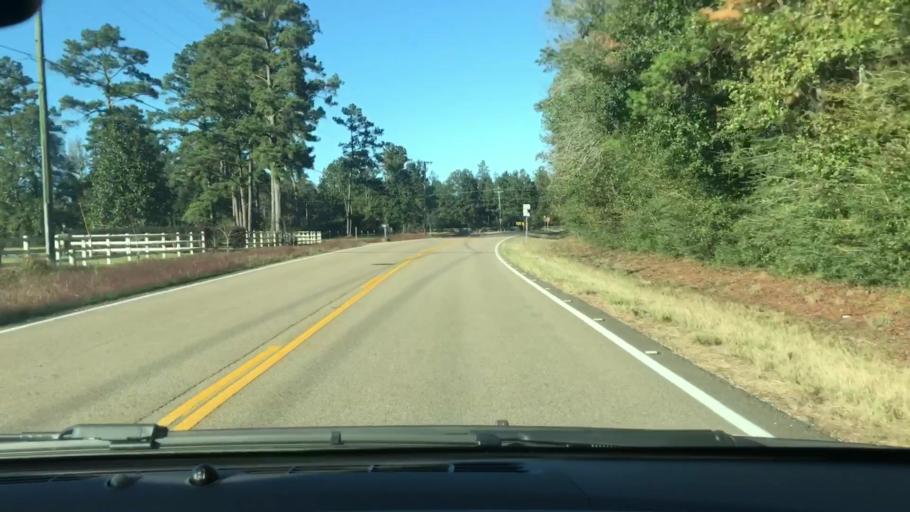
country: US
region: Louisiana
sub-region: Saint Tammany Parish
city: Abita Springs
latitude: 30.6365
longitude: -90.0156
